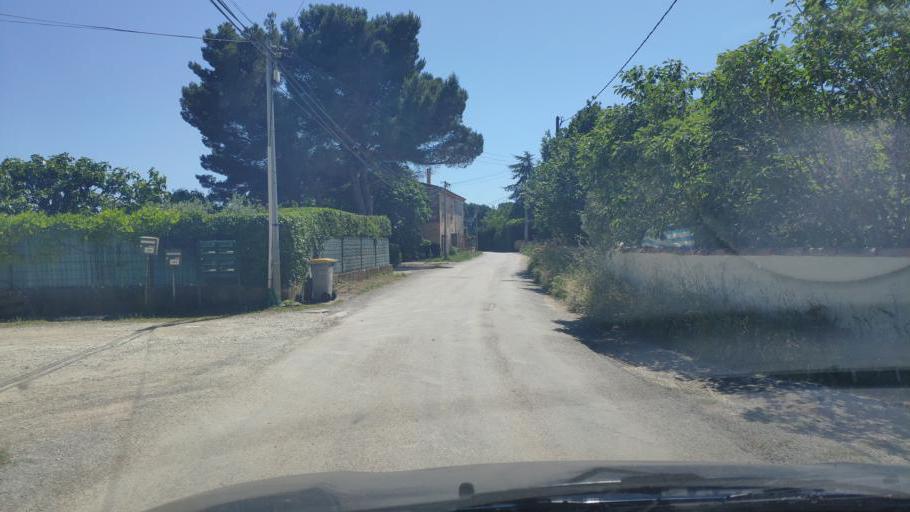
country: FR
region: Provence-Alpes-Cote d'Azur
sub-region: Departement du Vaucluse
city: Carpentras
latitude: 44.0728
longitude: 5.0551
